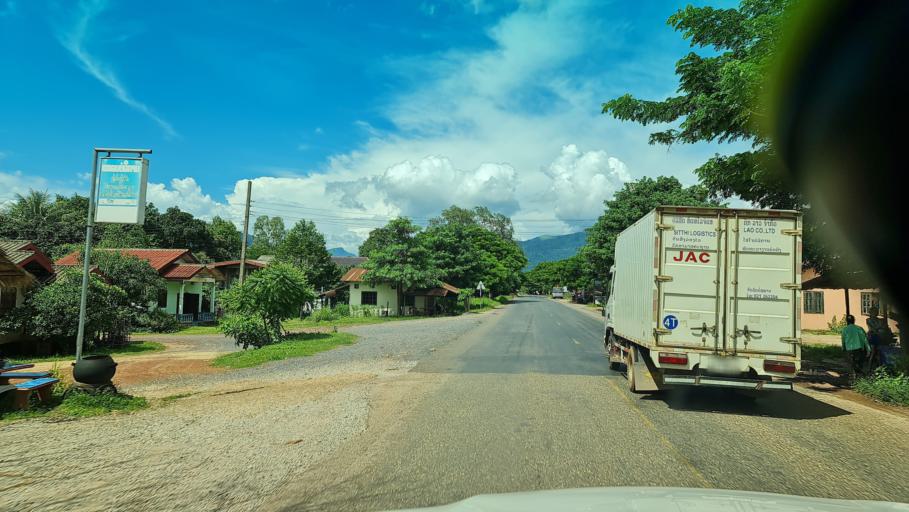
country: LA
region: Bolikhamxai
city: Pakkading
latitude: 18.2978
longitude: 104.0920
